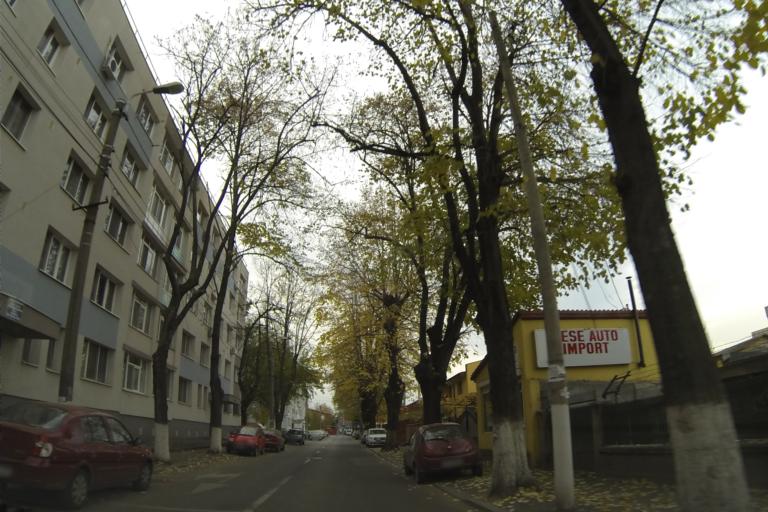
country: RO
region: Ilfov
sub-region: Comuna Chiajna
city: Rosu
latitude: 44.4359
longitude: 26.0104
